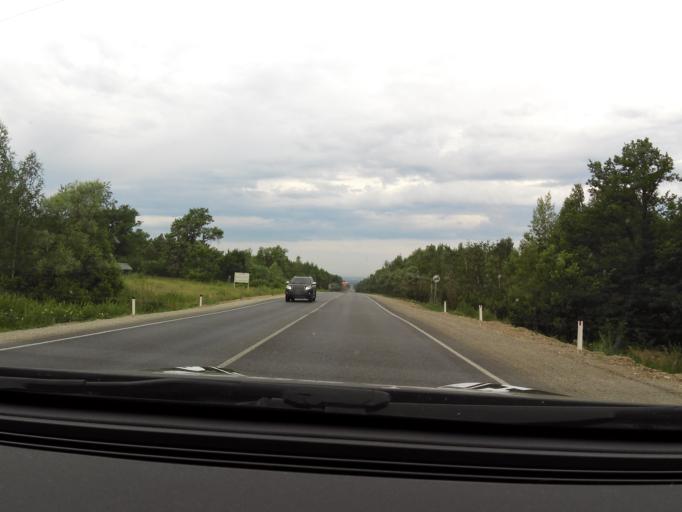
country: RU
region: Bashkortostan
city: Ulu-Telyak
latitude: 54.8411
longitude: 57.0534
